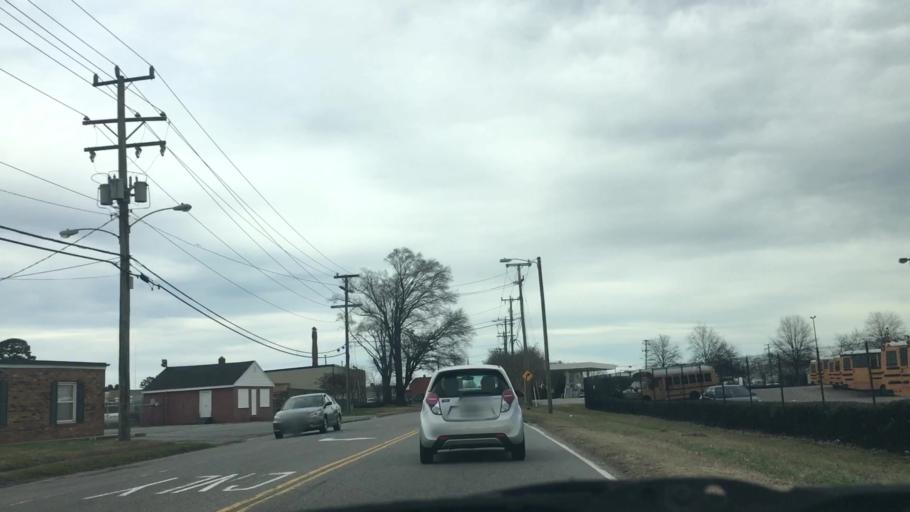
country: US
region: Virginia
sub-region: City of Norfolk
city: Norfolk
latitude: 36.8581
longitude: -76.2181
